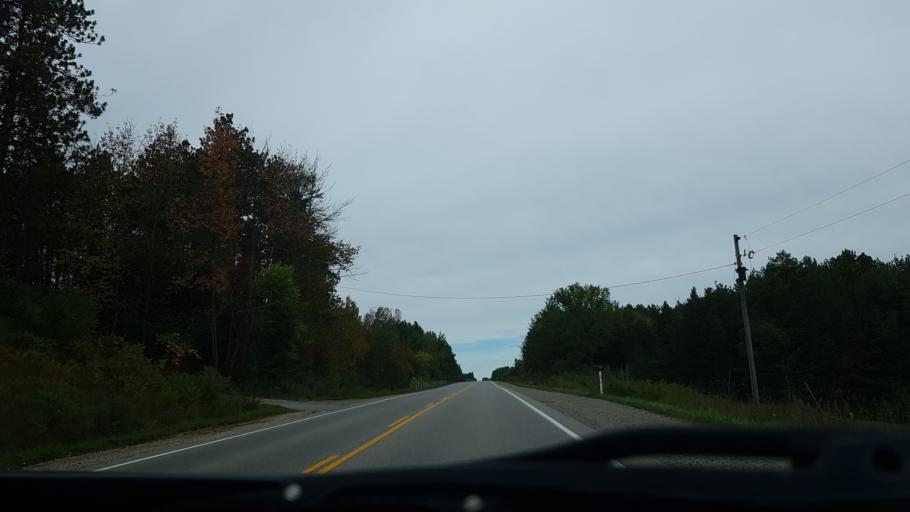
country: CA
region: Ontario
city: Orangeville
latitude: 44.0152
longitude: -80.0024
